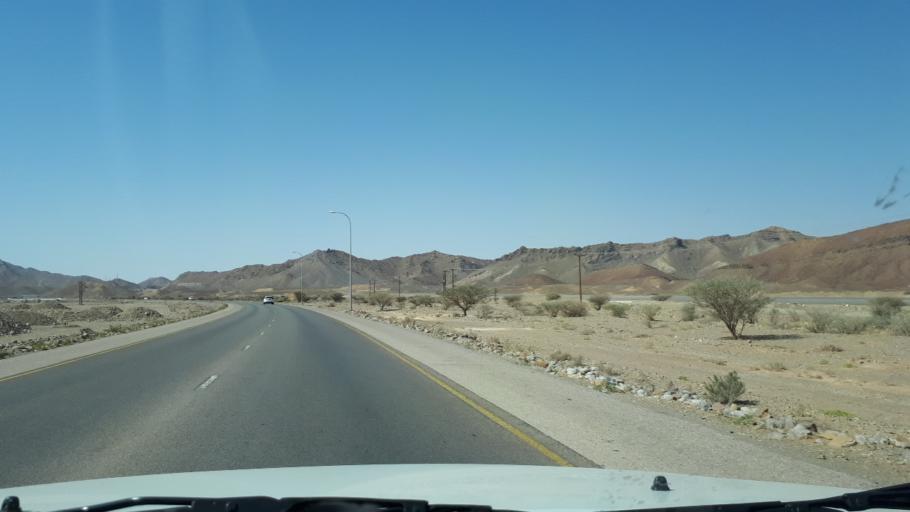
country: OM
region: Ash Sharqiyah
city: Sur
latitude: 22.3650
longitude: 59.3131
